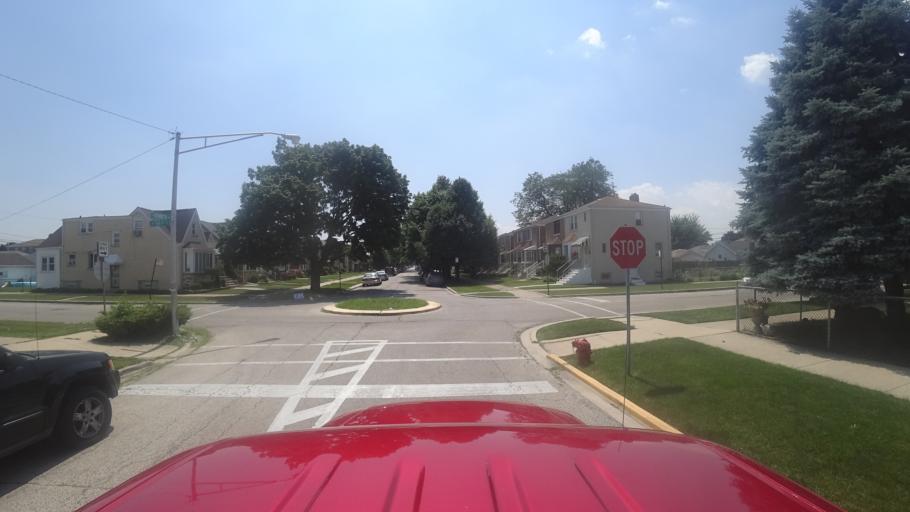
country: US
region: Illinois
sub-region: Cook County
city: Hometown
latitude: 41.7915
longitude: -87.7342
